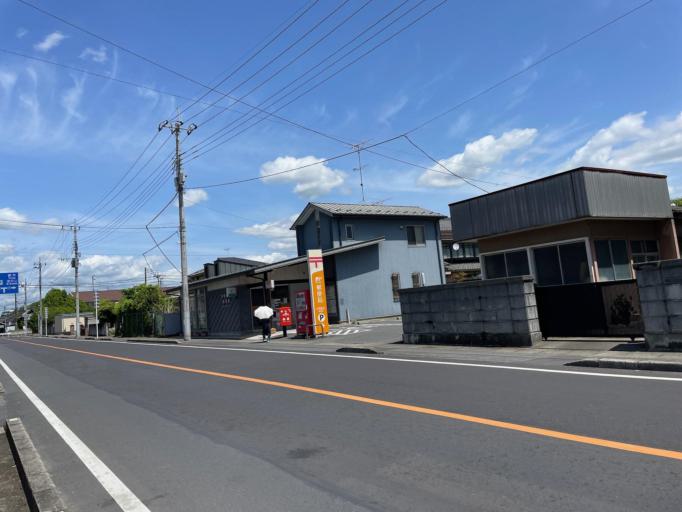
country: JP
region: Tochigi
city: Sano
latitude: 36.3209
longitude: 139.5847
